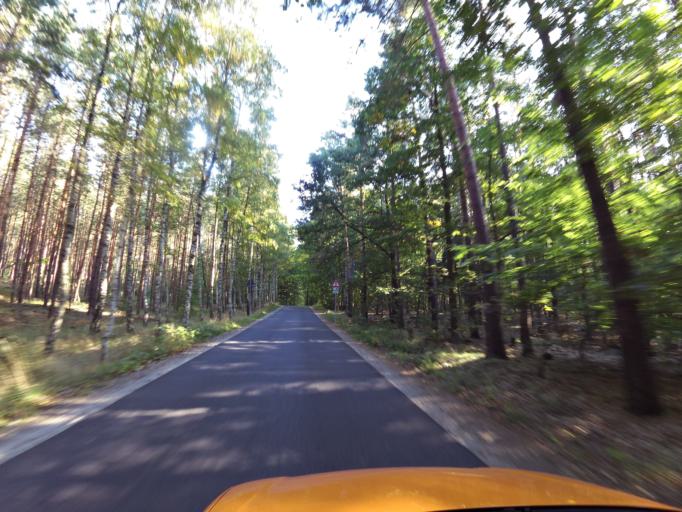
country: DE
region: Brandenburg
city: Potsdam
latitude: 52.4442
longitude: 13.0722
